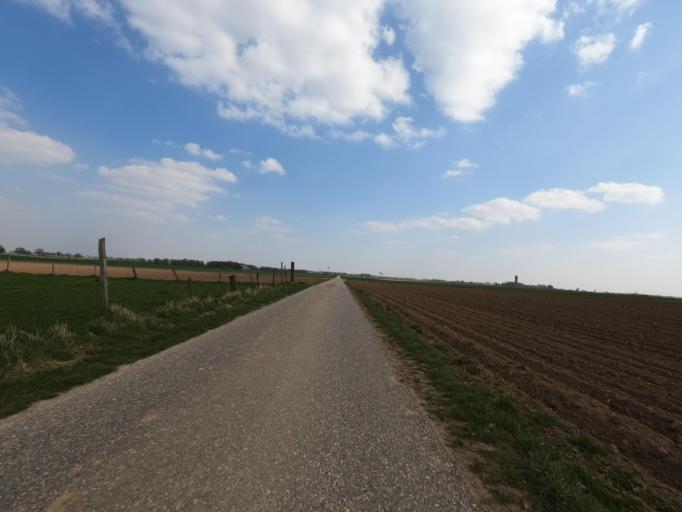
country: DE
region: North Rhine-Westphalia
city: Huckelhoven
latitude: 51.0792
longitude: 6.2540
